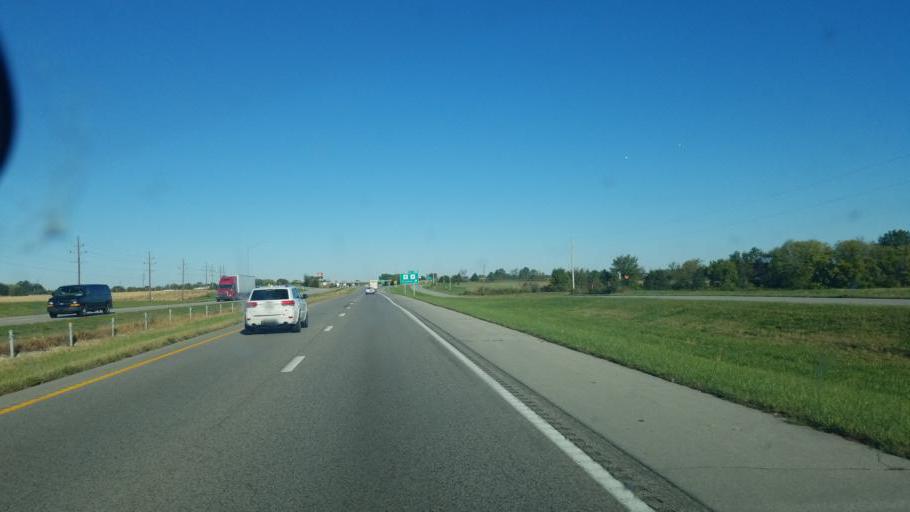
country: US
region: Missouri
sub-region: Warren County
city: Warrenton
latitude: 38.8343
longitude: -91.2192
